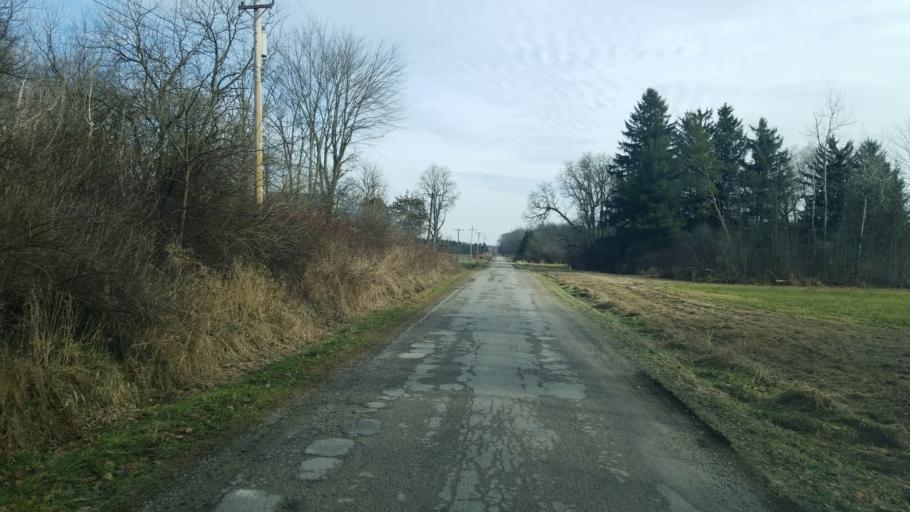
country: US
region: Ohio
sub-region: Ashtabula County
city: Roaming Shores
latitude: 41.6431
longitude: -80.8059
